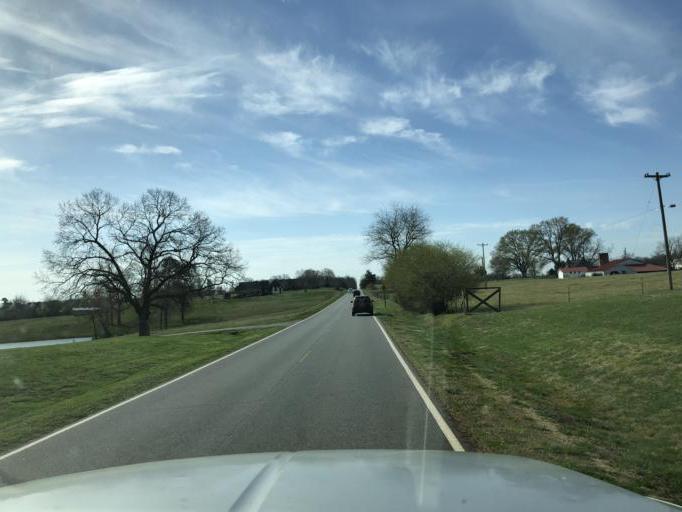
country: US
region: North Carolina
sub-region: Burke County
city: Salem
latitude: 35.4939
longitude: -81.6320
